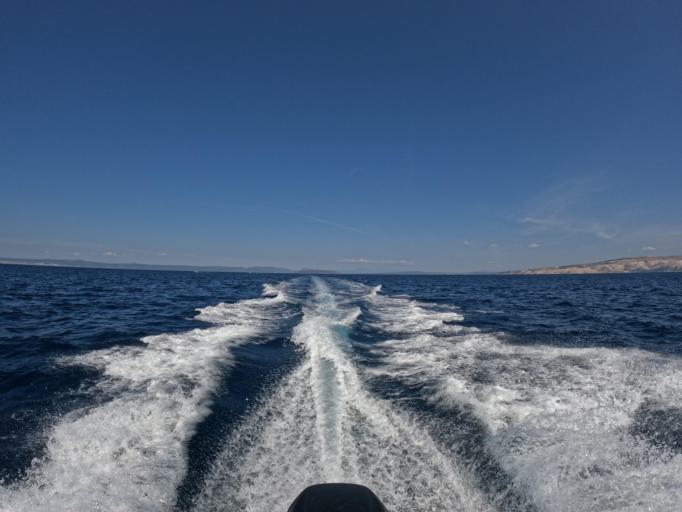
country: HR
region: Primorsko-Goranska
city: Lopar
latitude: 44.8858
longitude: 14.6513
